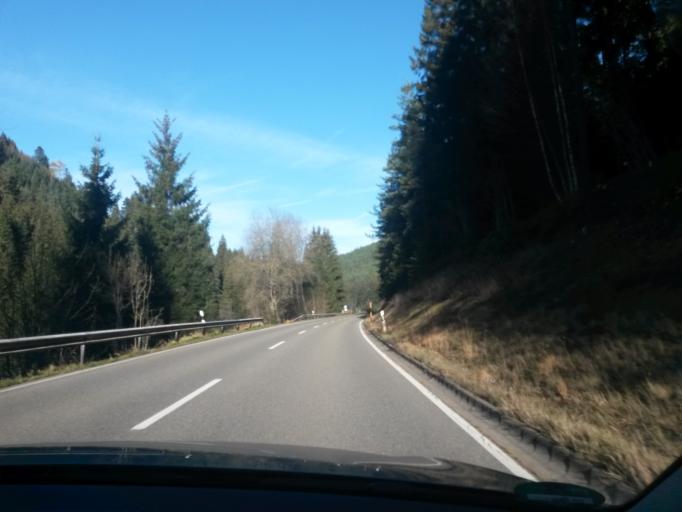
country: DE
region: Baden-Wuerttemberg
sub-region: Karlsruhe Region
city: Neuweiler
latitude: 48.6679
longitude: 8.5578
